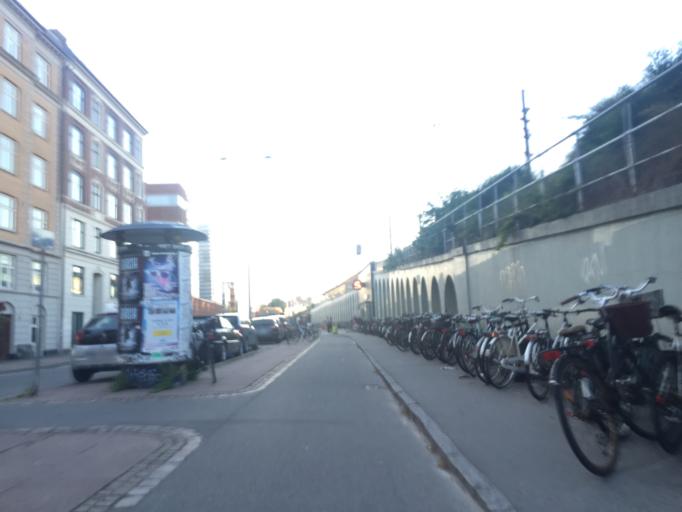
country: DK
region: Capital Region
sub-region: Kobenhavn
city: Christianshavn
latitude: 55.7040
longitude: 12.5910
